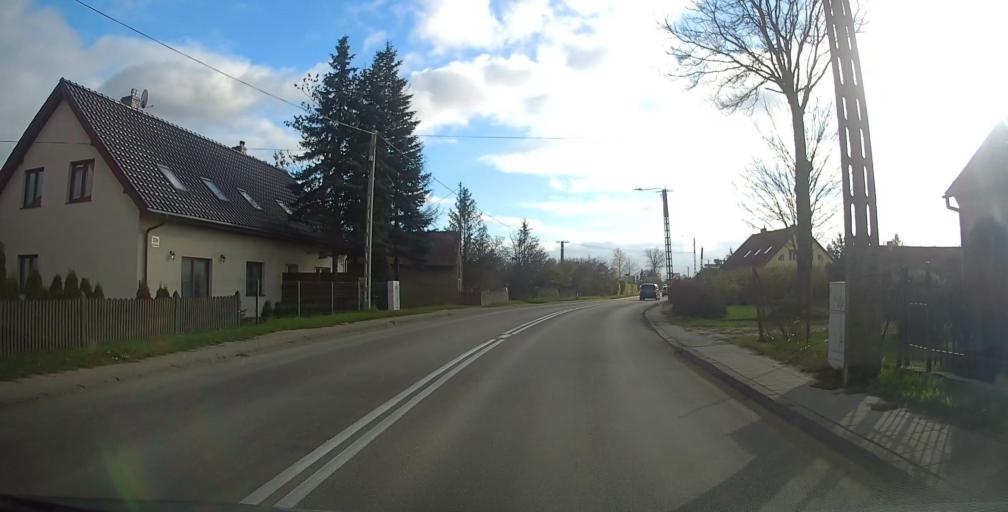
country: PL
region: Warmian-Masurian Voivodeship
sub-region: Powiat elcki
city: Elk
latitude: 53.7651
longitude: 22.3369
